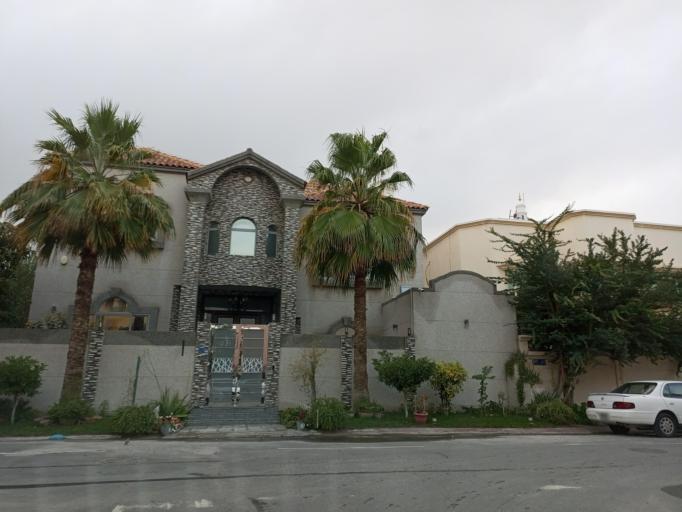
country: BH
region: Muharraq
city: Al Hadd
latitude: 26.2442
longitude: 50.6486
